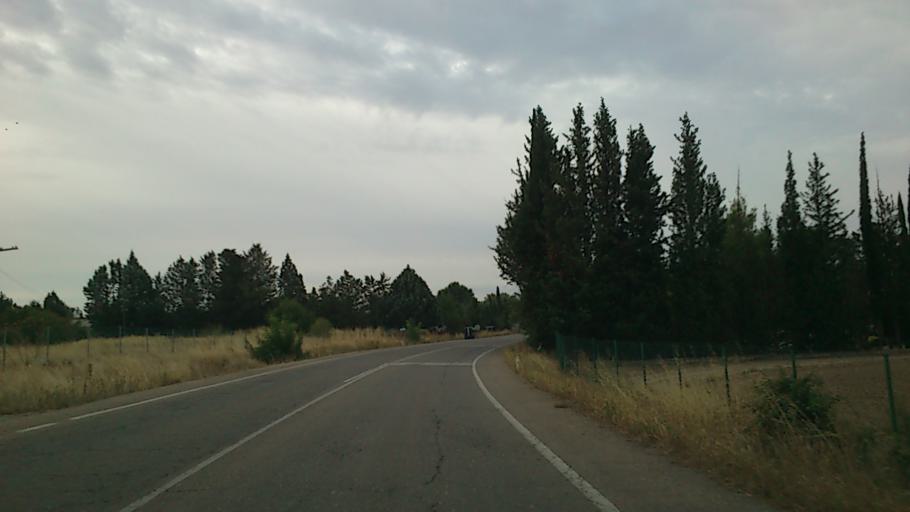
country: ES
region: Aragon
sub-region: Provincia de Zaragoza
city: Villanueva de Gallego
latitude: 41.7267
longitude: -0.8101
